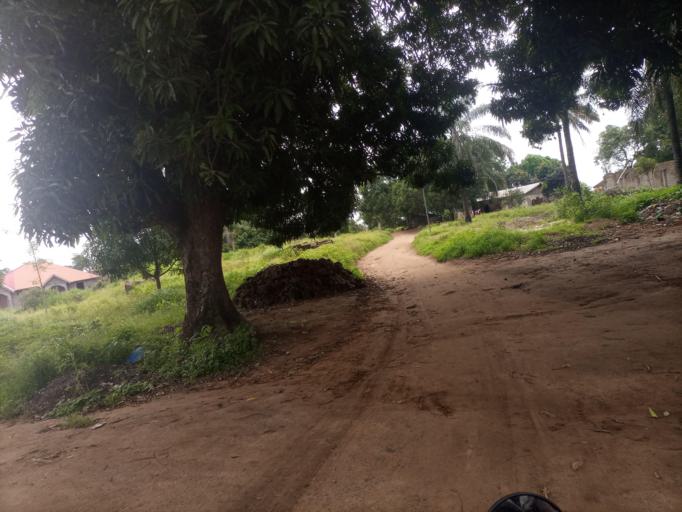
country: SL
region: Northern Province
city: Masoyila
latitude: 8.5698
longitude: -13.1610
